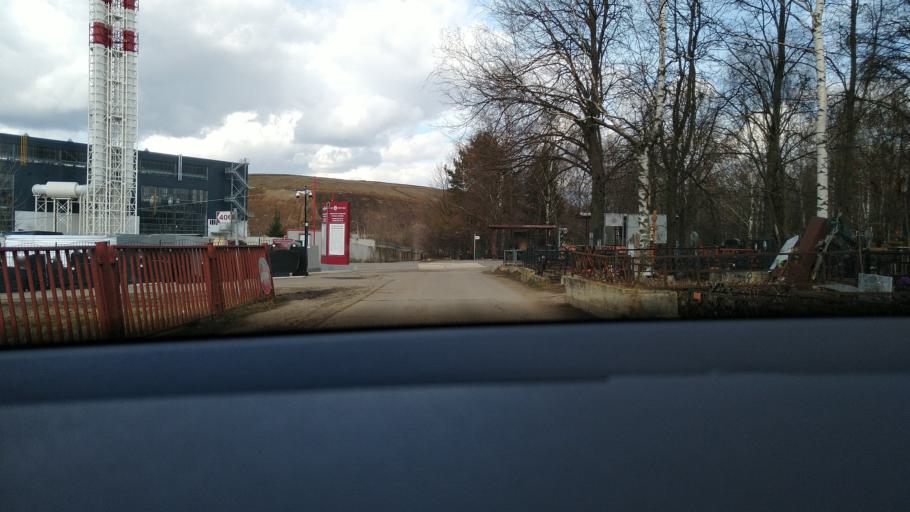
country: RU
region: Moskovskaya
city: Mosrentgen
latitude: 55.6061
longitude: 37.4339
